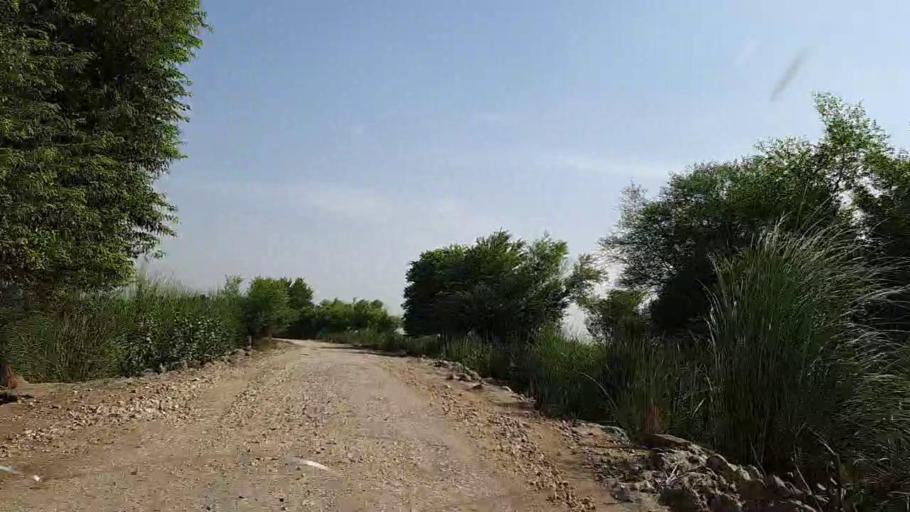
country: PK
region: Sindh
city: Khanpur
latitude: 27.7093
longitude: 69.3621
